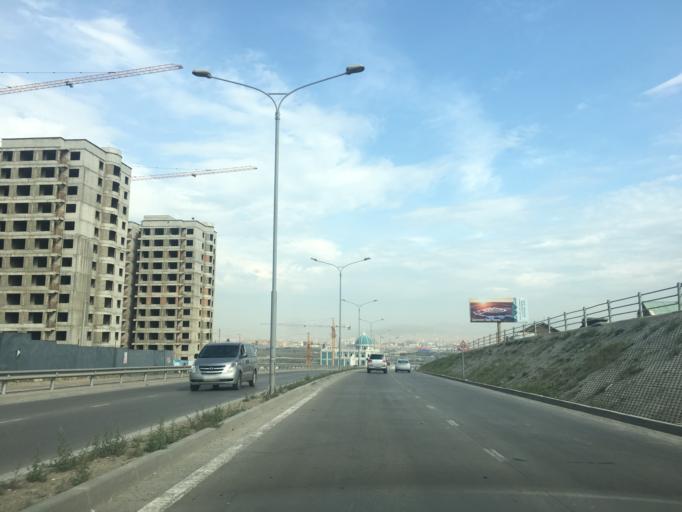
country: MN
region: Ulaanbaatar
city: Ulaanbaatar
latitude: 47.8679
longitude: 106.7859
